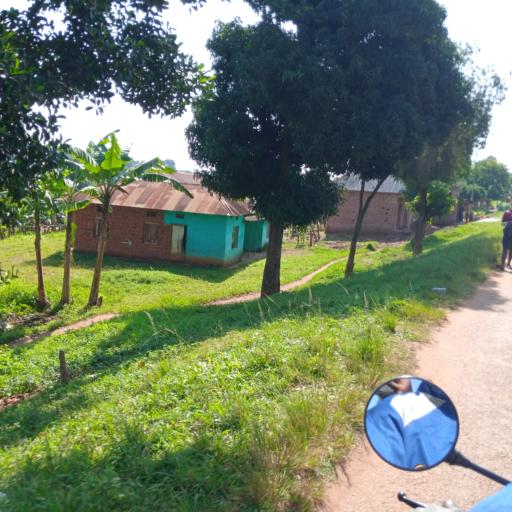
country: UG
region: Central Region
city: Masaka
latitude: -0.3781
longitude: 31.7094
